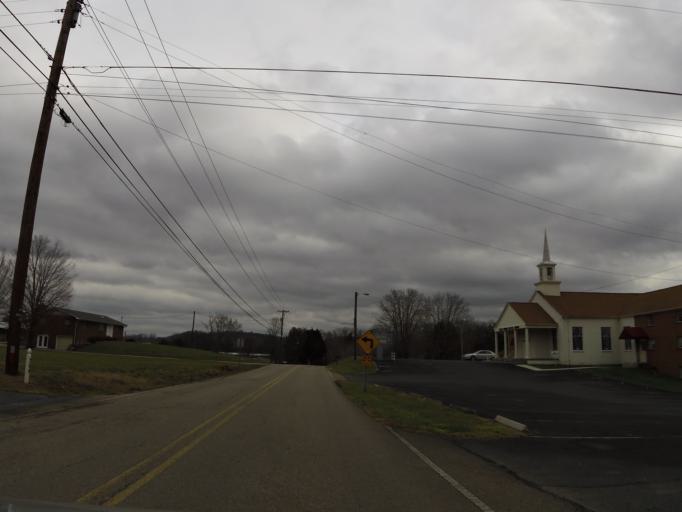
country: US
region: Tennessee
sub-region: Grainger County
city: Blaine
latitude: 36.1538
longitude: -83.7095
